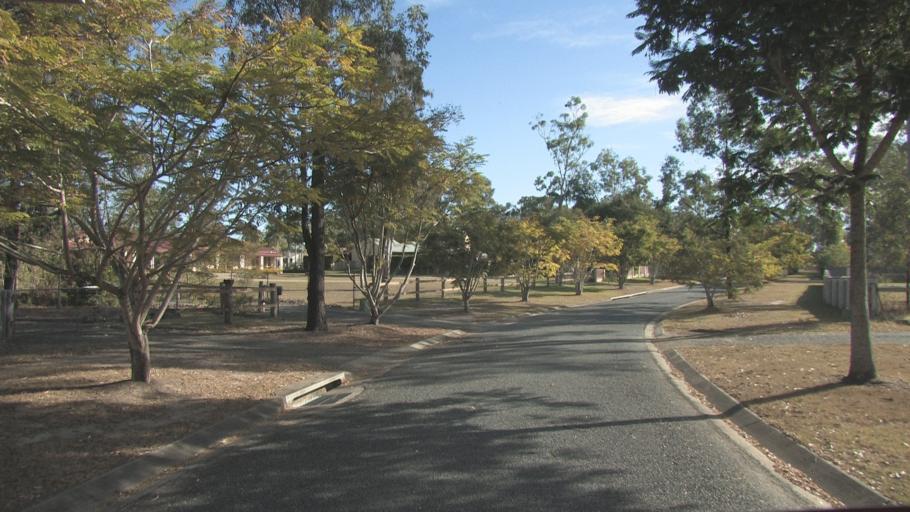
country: AU
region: Queensland
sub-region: Logan
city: North Maclean
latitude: -27.8062
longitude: 152.9633
